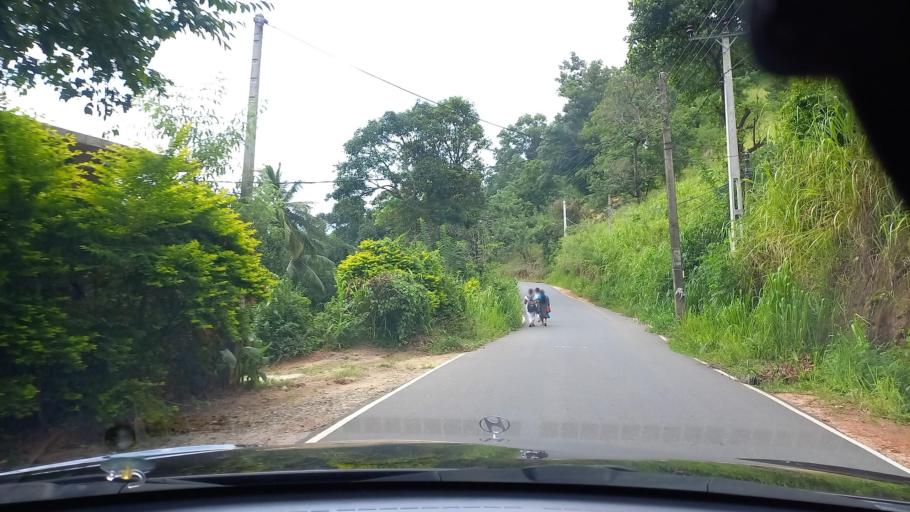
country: LK
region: Central
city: Gampola
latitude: 7.2213
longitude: 80.6078
